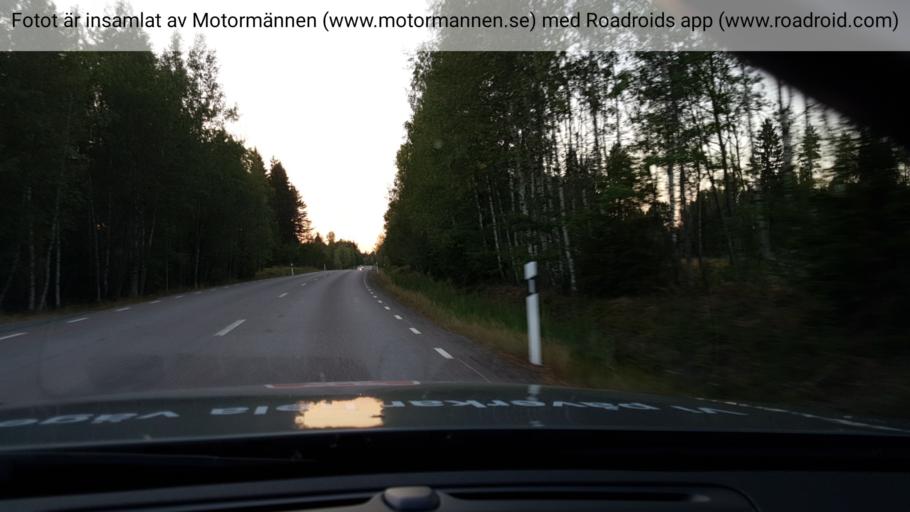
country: SE
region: Uppsala
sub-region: Heby Kommun
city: OEstervala
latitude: 60.0605
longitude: 17.2222
